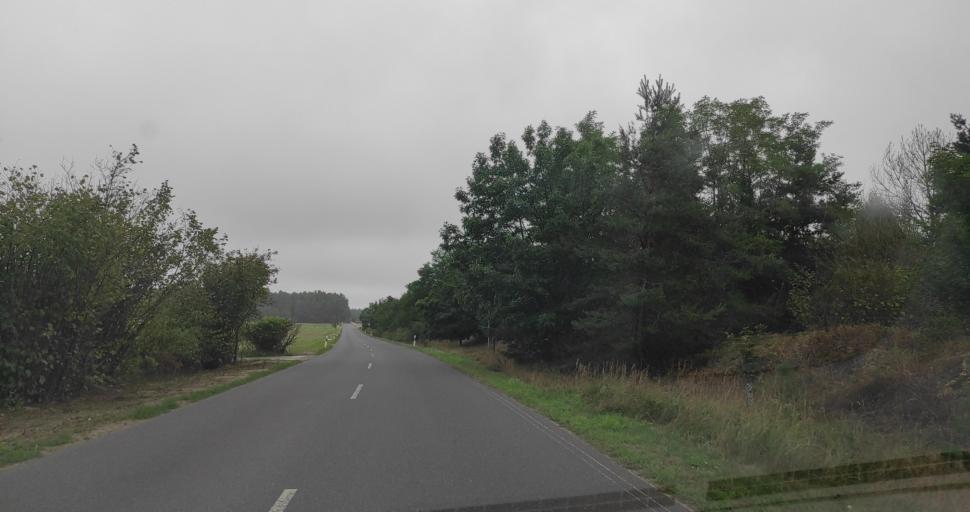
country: DE
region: Brandenburg
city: Forst
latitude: 51.6992
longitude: 14.5599
